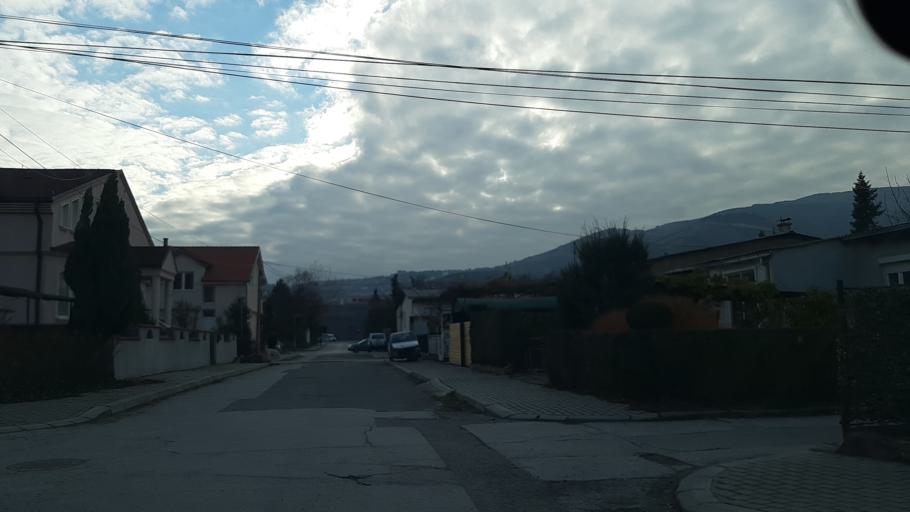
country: MK
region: Kisela Voda
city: Usje
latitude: 41.9770
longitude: 21.4544
